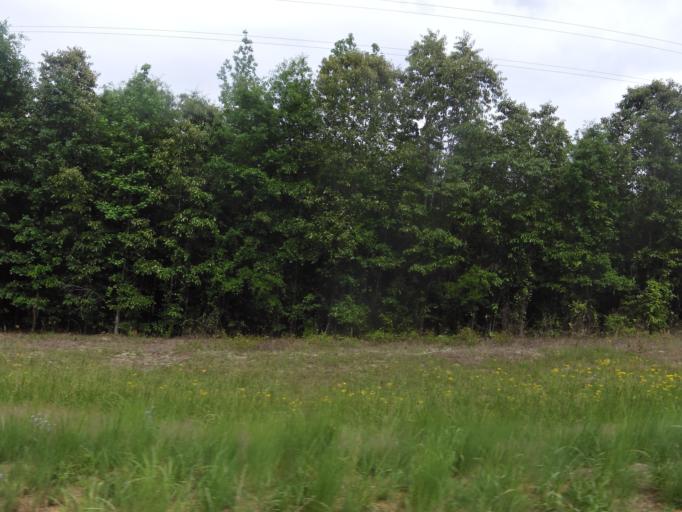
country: US
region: Georgia
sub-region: McDuffie County
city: Thomson
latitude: 33.4262
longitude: -82.4861
